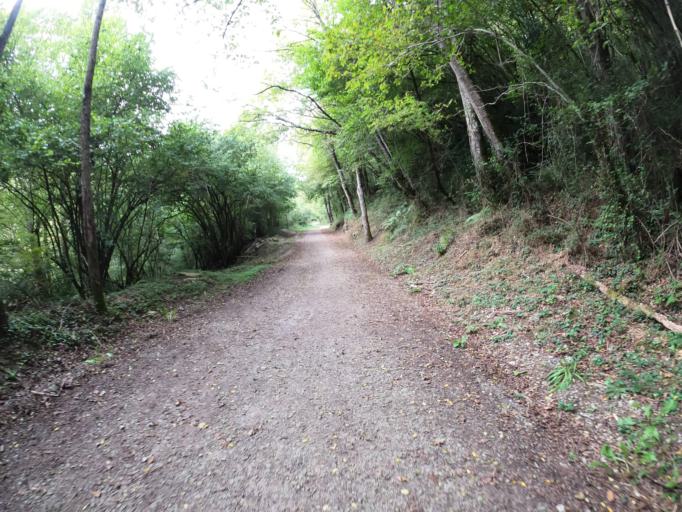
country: ES
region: Navarre
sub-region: Provincia de Navarra
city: Lekunberri
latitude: 42.9856
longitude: -1.8741
